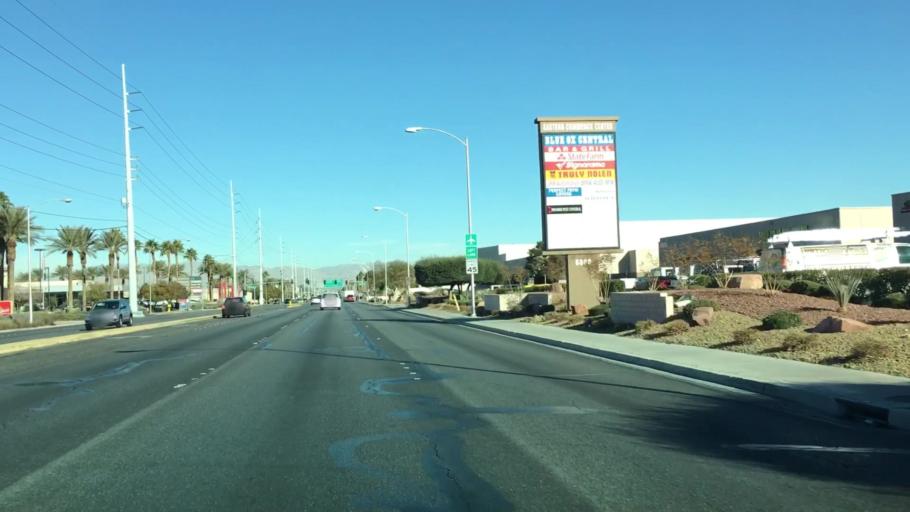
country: US
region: Nevada
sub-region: Clark County
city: Paradise
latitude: 36.0801
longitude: -115.1186
